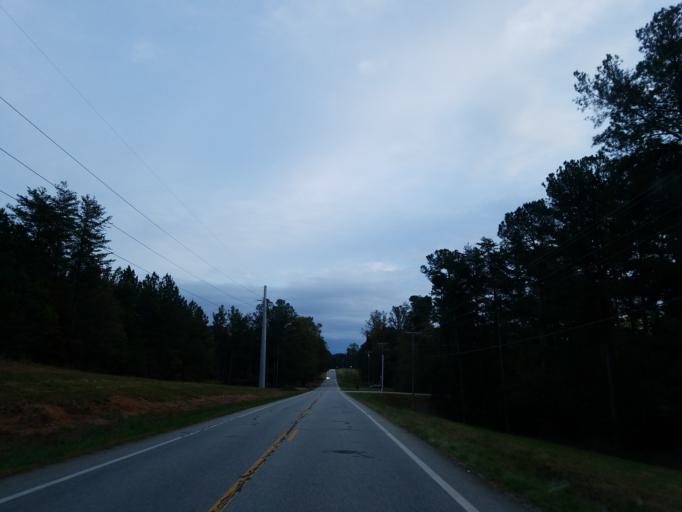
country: US
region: Georgia
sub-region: Dawson County
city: Dawsonville
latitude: 34.4532
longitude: -84.1711
